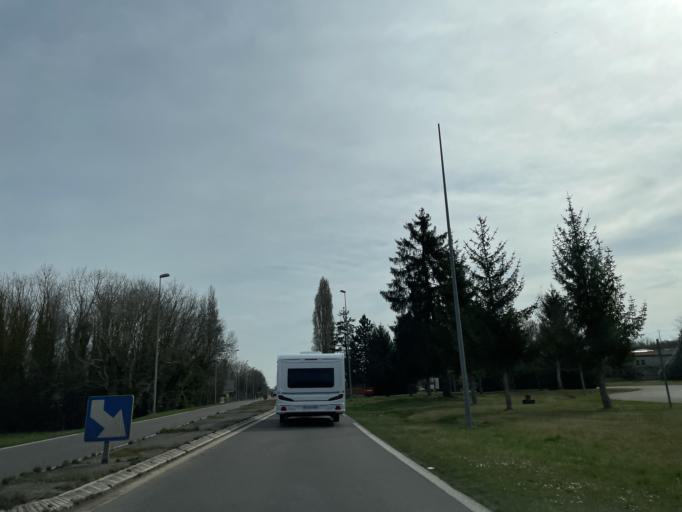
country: FR
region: Champagne-Ardenne
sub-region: Departement de l'Aube
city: Romilly-sur-Seine
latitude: 48.5147
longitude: 3.6643
